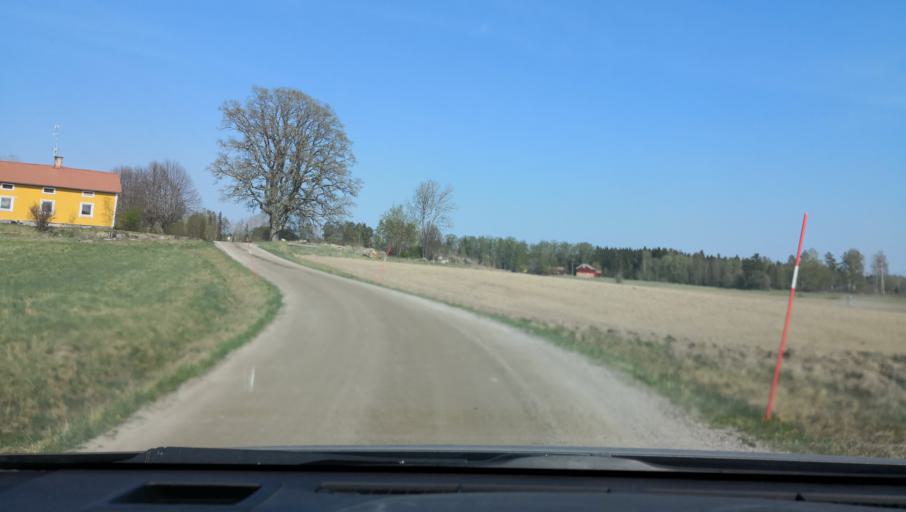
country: SE
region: Vaestmanland
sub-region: Sala Kommun
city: Sala
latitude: 60.0069
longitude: 16.7254
